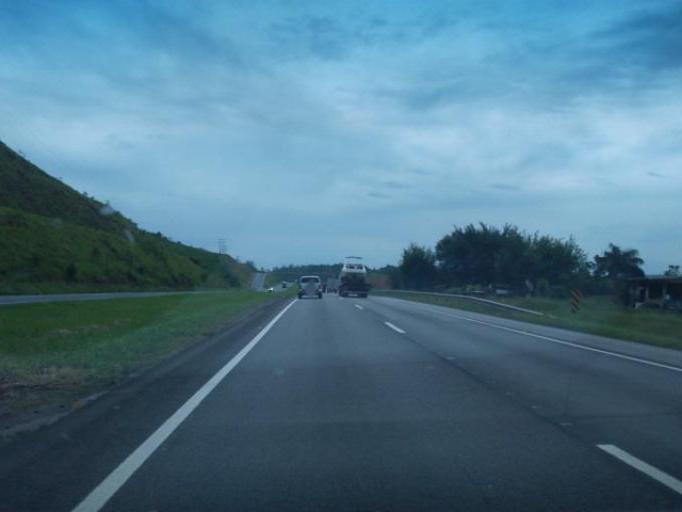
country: BR
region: Sao Paulo
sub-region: Juquia
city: Juquia
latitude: -24.3273
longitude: -47.5692
